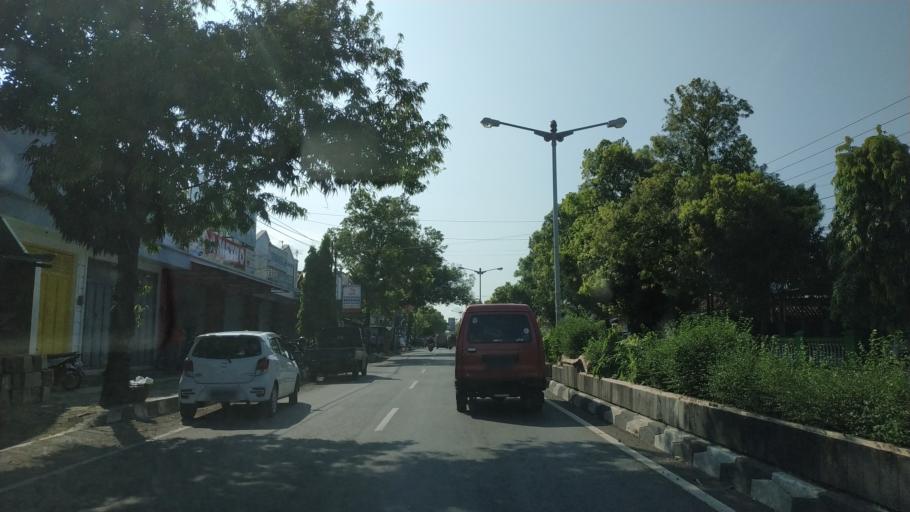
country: ID
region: Central Java
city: Petarukan
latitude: -6.8934
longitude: 109.4085
